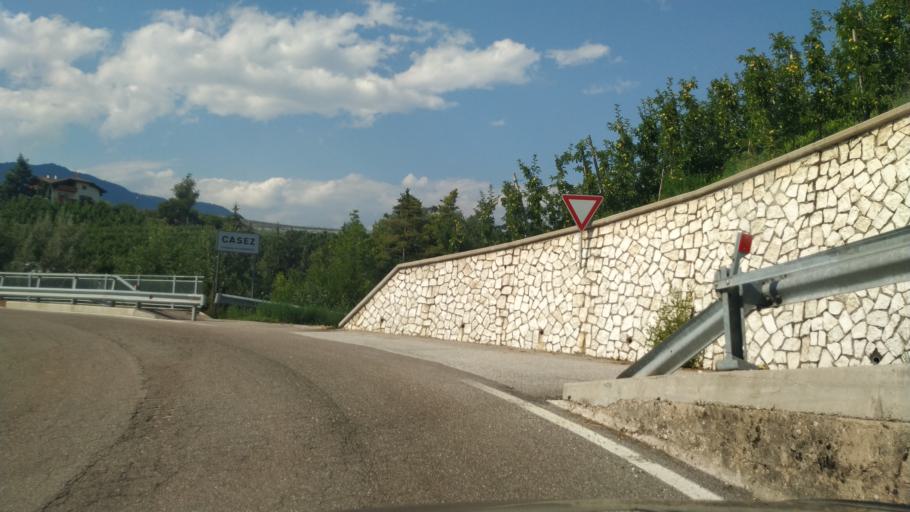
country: IT
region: Trentino-Alto Adige
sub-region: Provincia di Trento
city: Sanzeno
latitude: 46.3736
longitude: 11.0805
